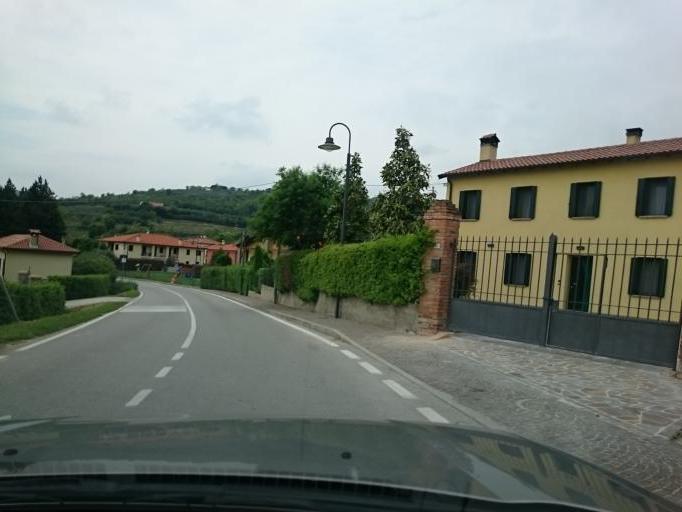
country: IT
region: Veneto
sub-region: Provincia di Padova
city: Arqua Petrarca
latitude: 45.2657
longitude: 11.7140
